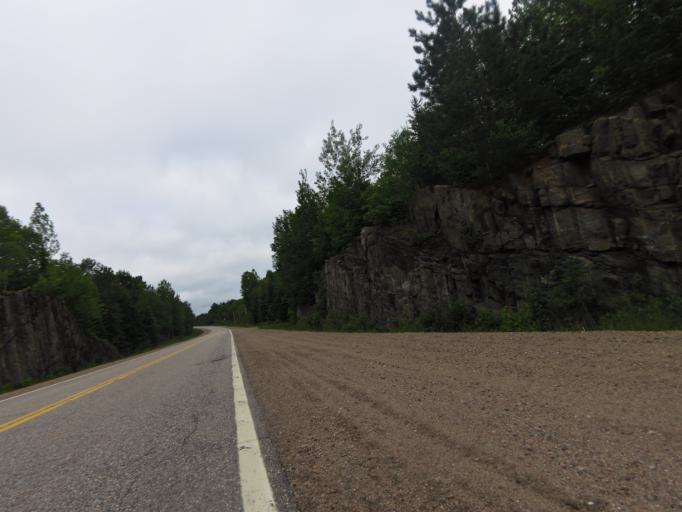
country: CA
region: Quebec
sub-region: Outaouais
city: Shawville
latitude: 45.9140
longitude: -76.3282
